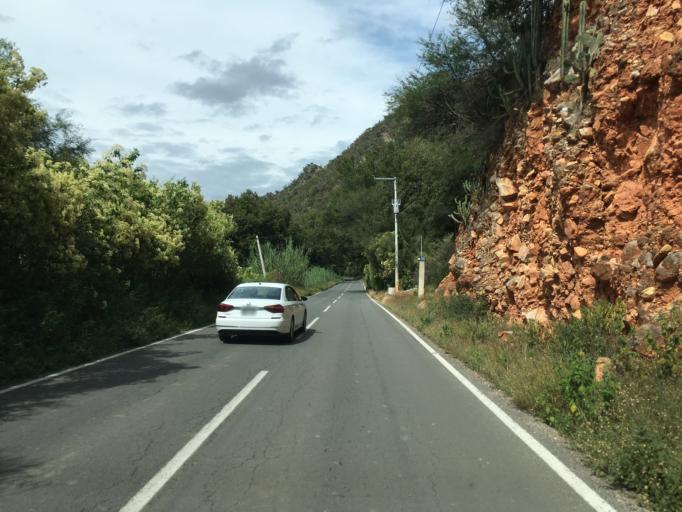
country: MX
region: Hidalgo
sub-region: San Agustin Metzquititlan
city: Mezquititlan
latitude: 20.5342
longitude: -98.7193
